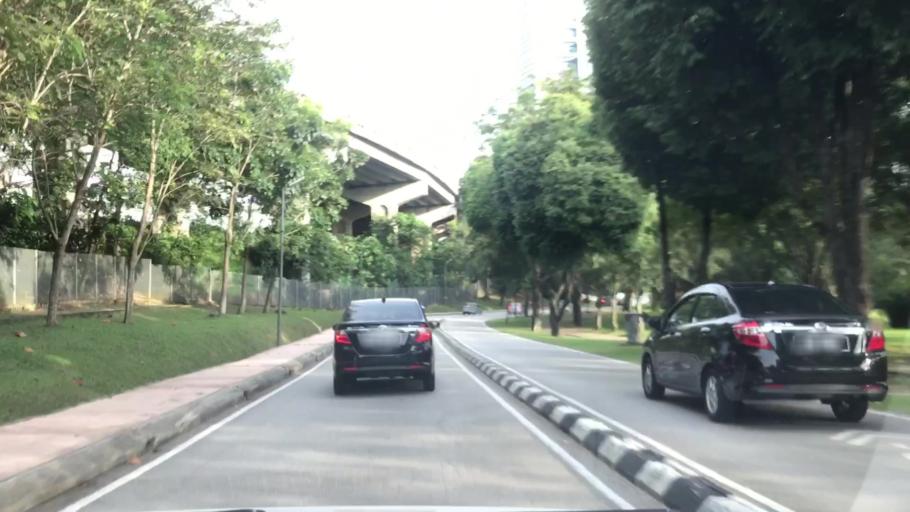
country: MY
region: Kuala Lumpur
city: Kuala Lumpur
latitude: 3.1202
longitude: 101.6610
